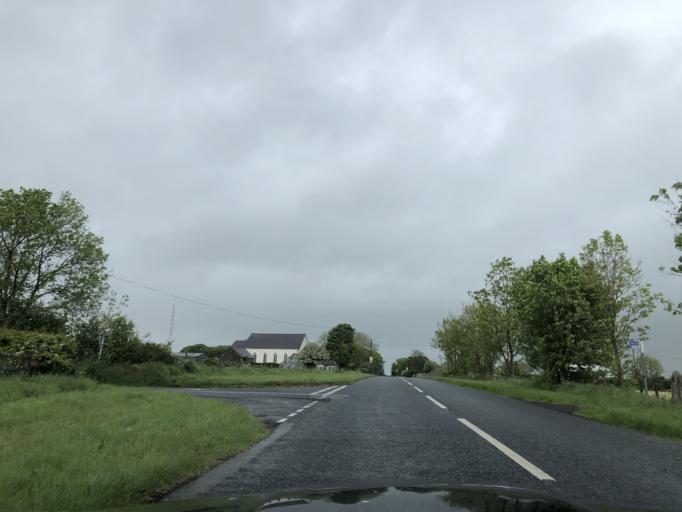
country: GB
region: Northern Ireland
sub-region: Moyle District
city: Ballycastle
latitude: 55.1767
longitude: -6.3323
